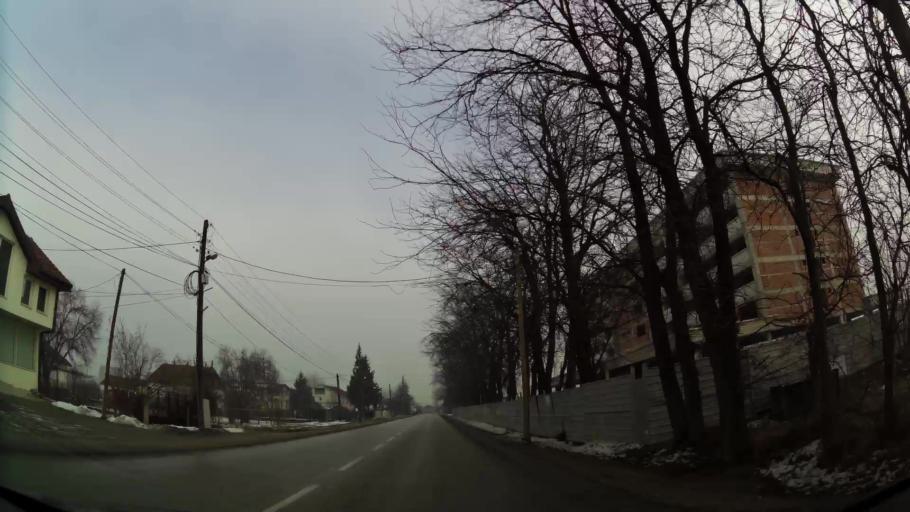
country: MK
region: Ilinden
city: Ilinden
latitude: 41.9958
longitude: 21.5663
